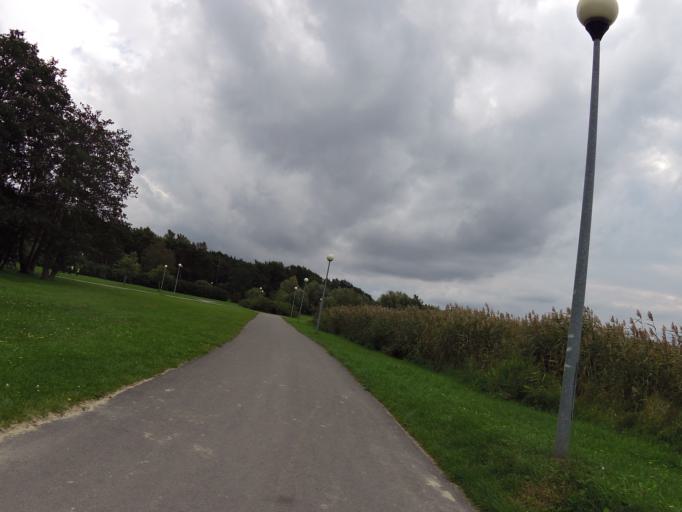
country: EE
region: Harju
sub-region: Tallinna linn
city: Tallinn
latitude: 59.4387
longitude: 24.6825
